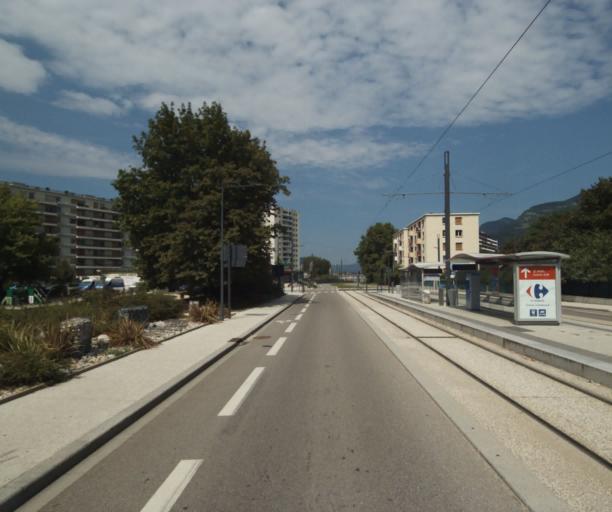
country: FR
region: Rhone-Alpes
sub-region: Departement de l'Isere
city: Saint-Egreve
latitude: 45.2353
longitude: 5.6760
